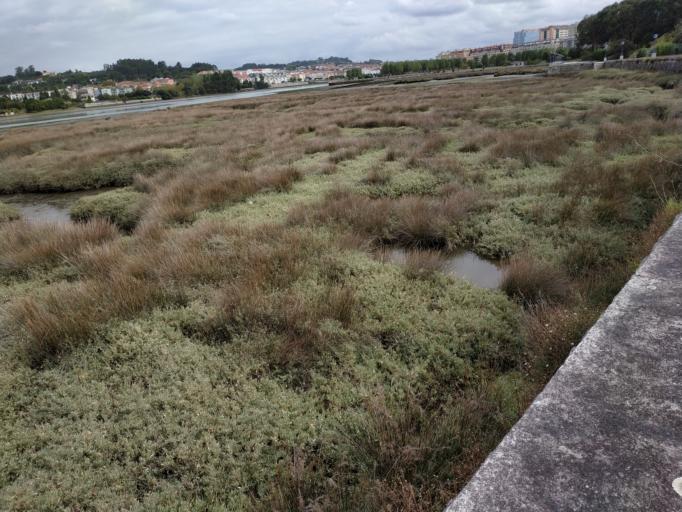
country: ES
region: Galicia
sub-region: Provincia da Coruna
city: Culleredo
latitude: 43.3223
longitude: -8.3742
